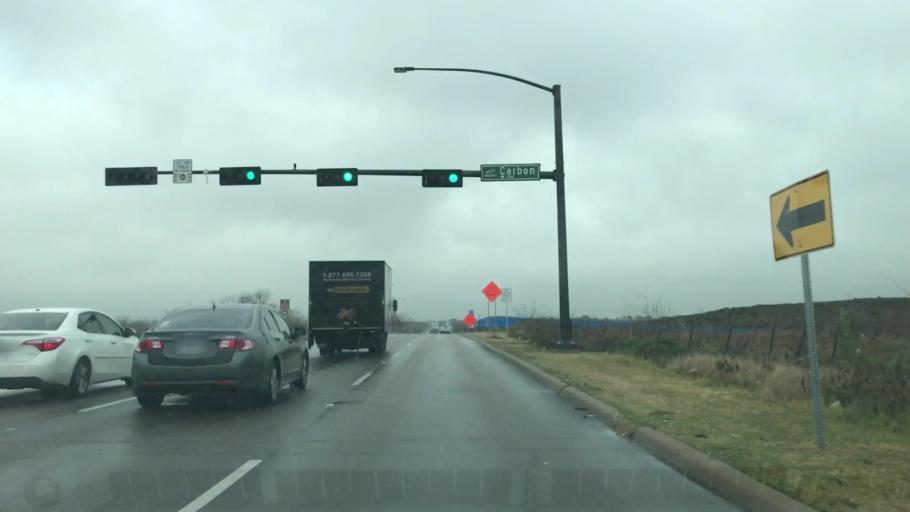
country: US
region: Texas
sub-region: Dallas County
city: Coppell
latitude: 32.8801
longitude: -96.9913
